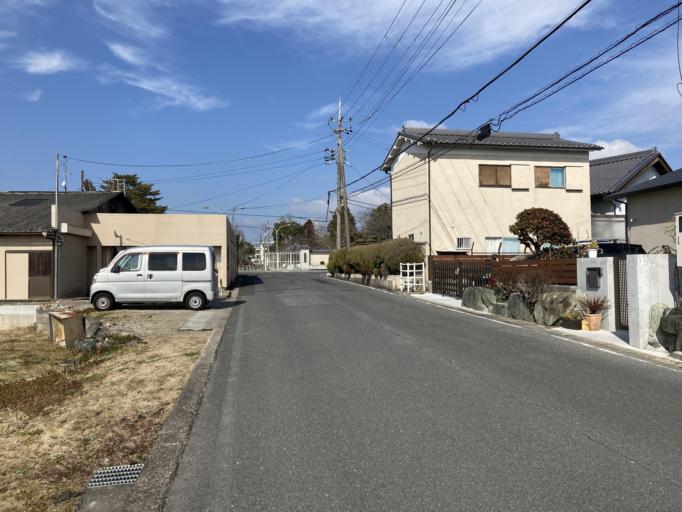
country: JP
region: Nara
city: Nara-shi
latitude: 34.6964
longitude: 135.8064
